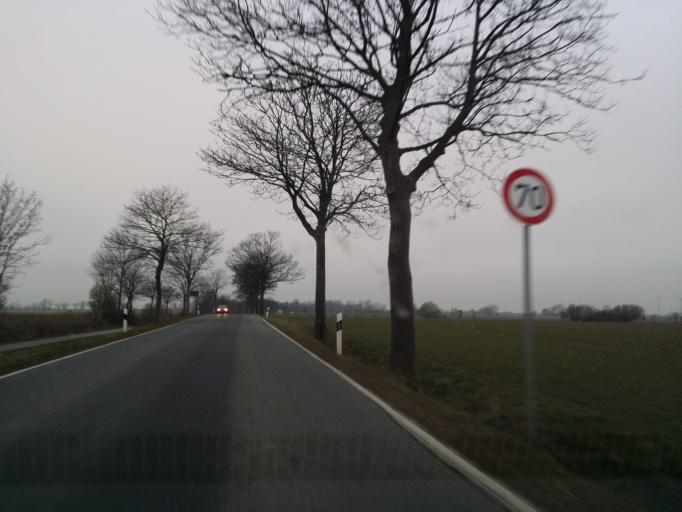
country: DE
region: Schleswig-Holstein
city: Fehmarn
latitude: 54.4570
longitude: 11.1339
